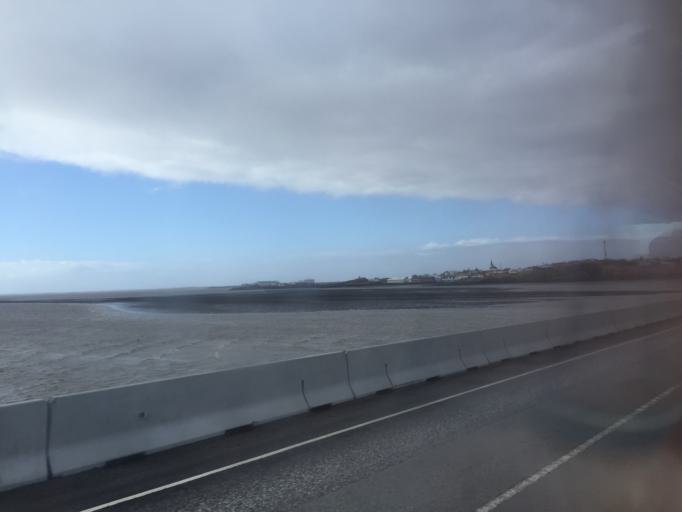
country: IS
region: West
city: Borgarnes
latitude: 64.5355
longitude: -21.8972
